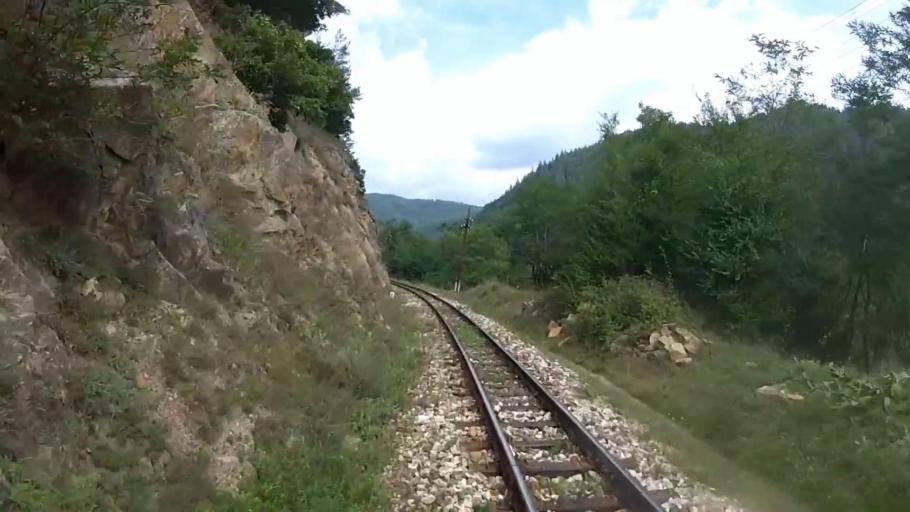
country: BG
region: Blagoevgrad
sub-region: Obshtina Yakoruda
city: Yakoruda
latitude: 42.0427
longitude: 23.7205
